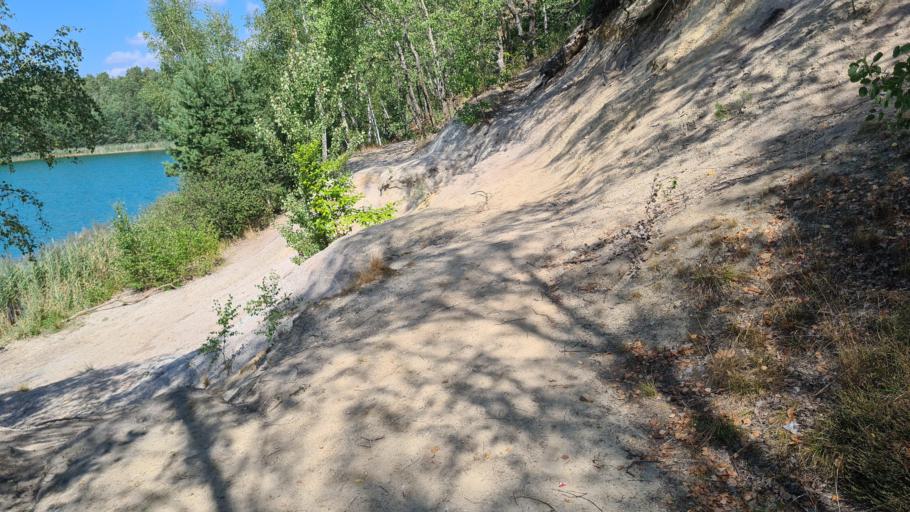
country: DE
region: Brandenburg
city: Sallgast
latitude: 51.5737
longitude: 13.8432
